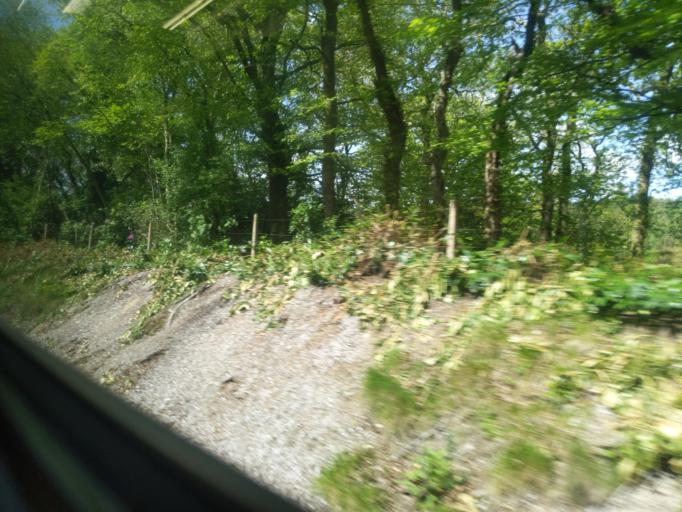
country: GB
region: England
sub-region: Cornwall
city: Liskeard
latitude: 50.4529
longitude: -4.5626
